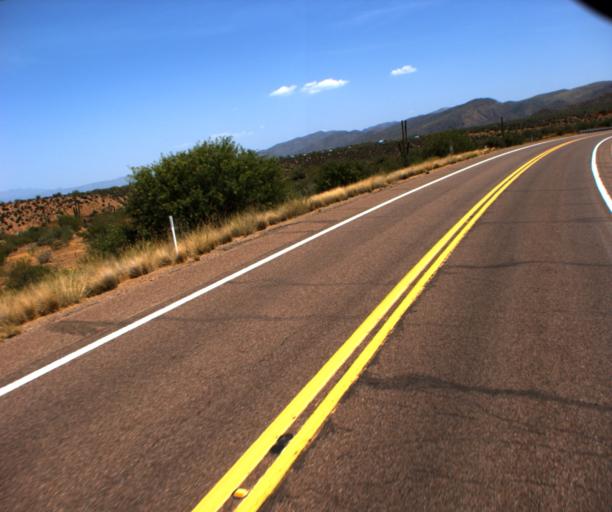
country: US
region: Arizona
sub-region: Gila County
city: Tonto Basin
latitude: 33.7335
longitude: -111.2118
